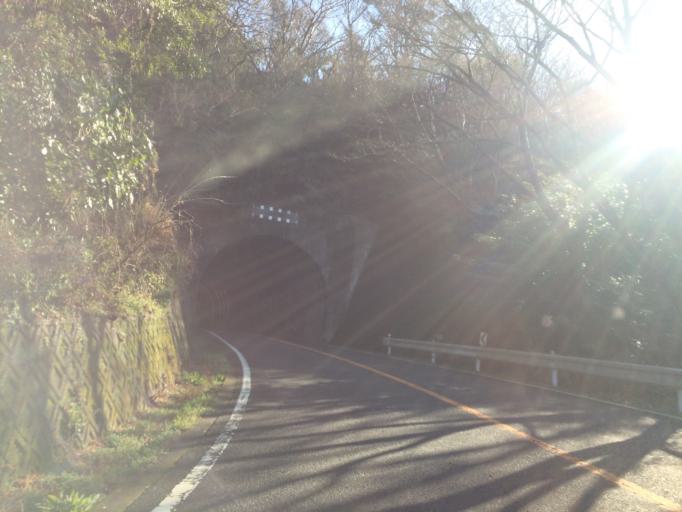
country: JP
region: Shizuoka
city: Shizuoka-shi
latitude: 34.9715
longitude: 138.4609
